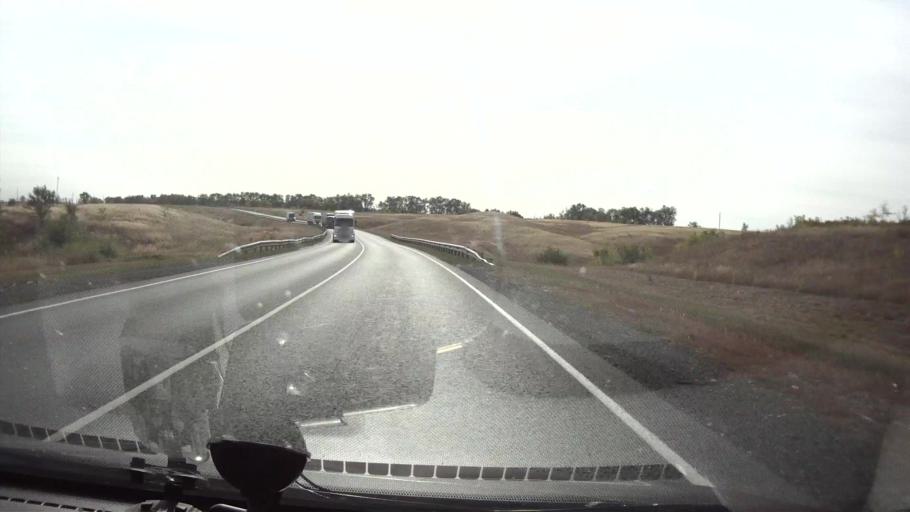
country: RU
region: Saratov
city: Balakovo
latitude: 52.1280
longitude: 47.7566
